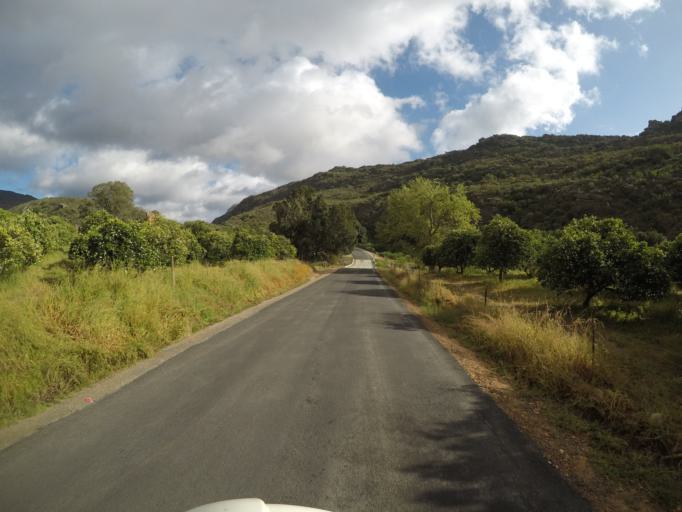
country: ZA
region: Western Cape
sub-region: West Coast District Municipality
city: Clanwilliam
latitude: -32.4144
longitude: 18.9230
